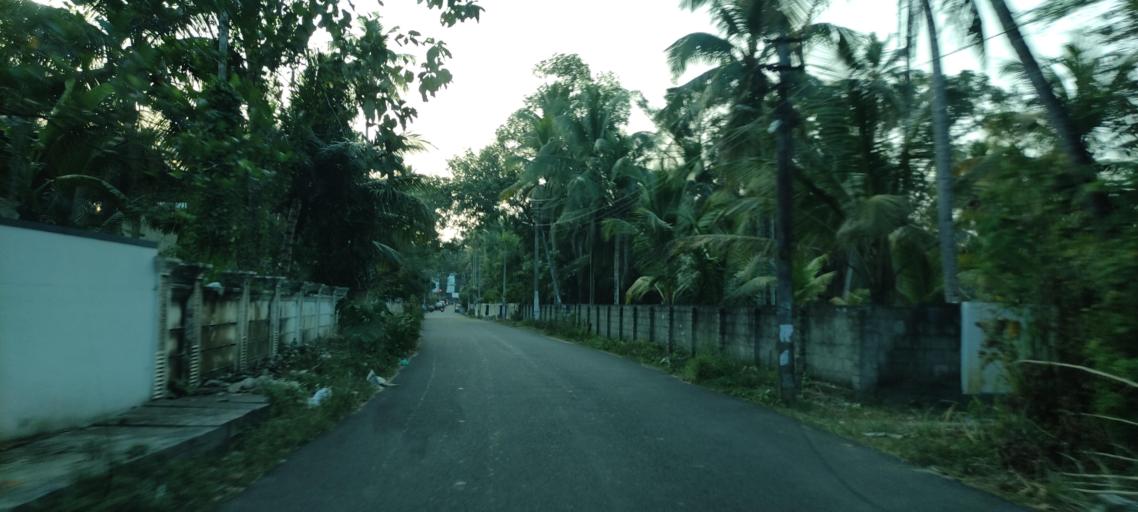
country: IN
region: Kerala
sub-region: Alappuzha
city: Kayankulam
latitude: 9.1362
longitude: 76.5260
